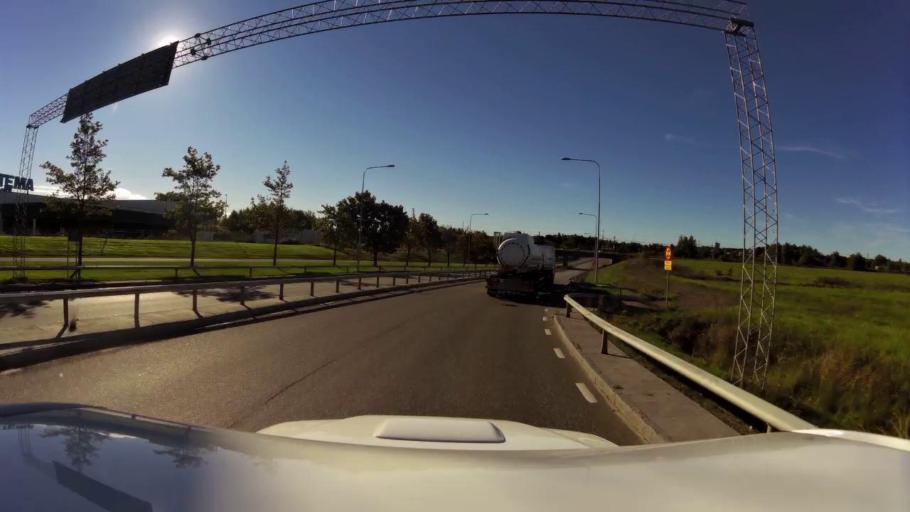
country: SE
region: OEstergoetland
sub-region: Linkopings Kommun
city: Linkoping
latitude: 58.4167
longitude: 15.6558
